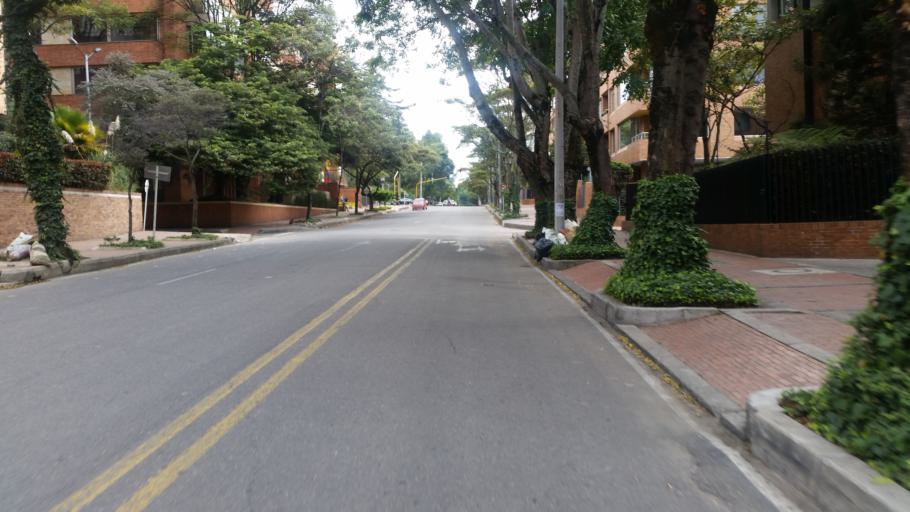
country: CO
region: Bogota D.C.
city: Barrio San Luis
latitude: 4.6770
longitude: -74.0432
